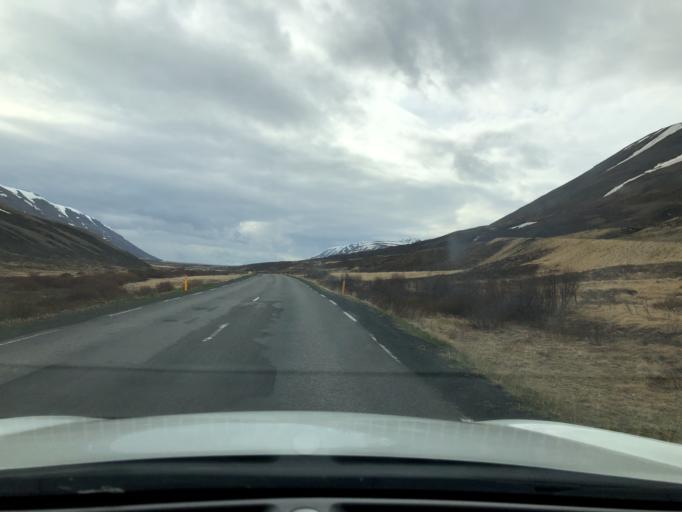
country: IS
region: Northeast
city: Akureyri
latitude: 65.7404
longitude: -17.8675
